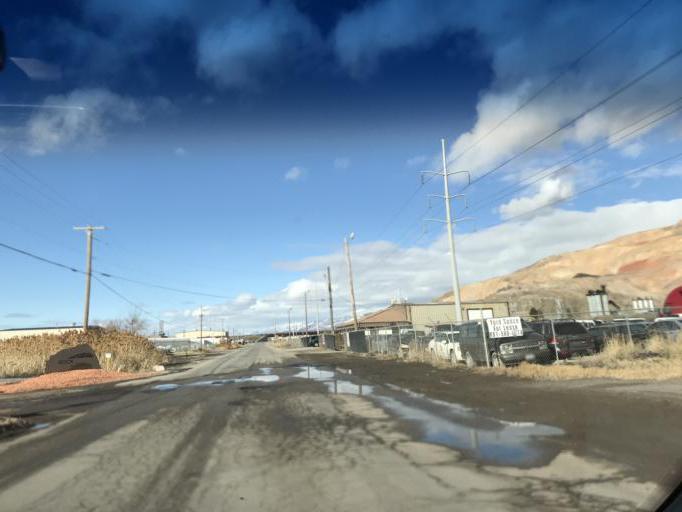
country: US
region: Utah
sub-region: Davis County
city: North Salt Lake
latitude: 40.8085
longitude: -111.9208
